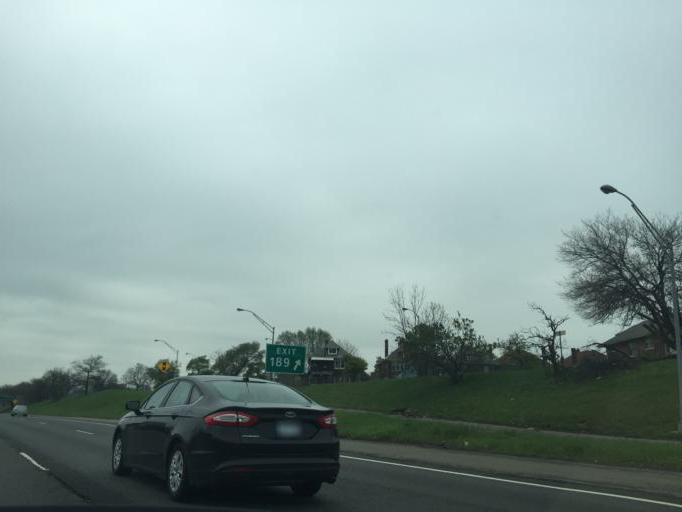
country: US
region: Michigan
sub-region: Wayne County
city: Highland Park
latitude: 42.3579
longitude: -83.1148
